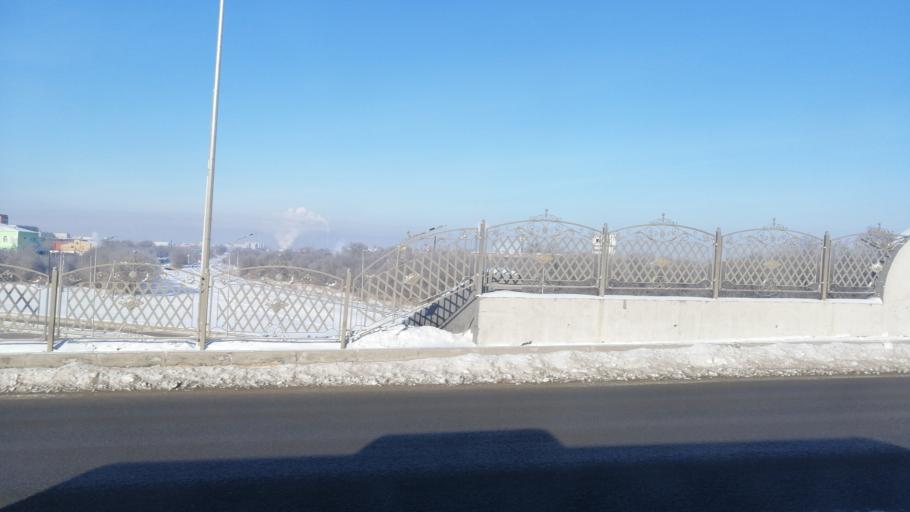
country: KZ
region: Aqtoebe
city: Aqtobe
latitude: 50.2948
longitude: 57.1790
